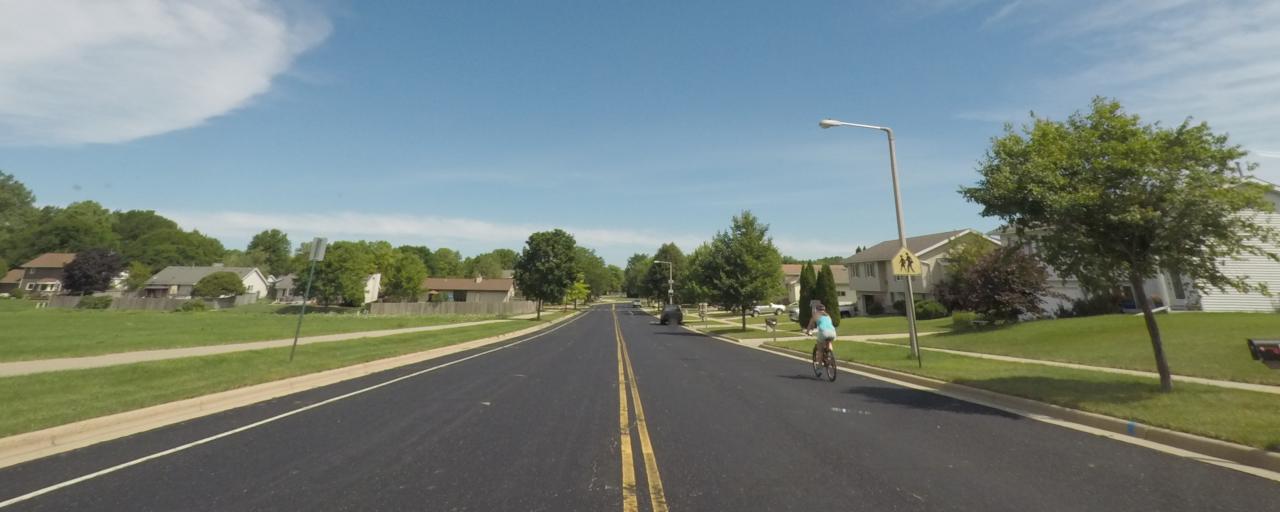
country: US
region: Wisconsin
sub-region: Dane County
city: McFarland
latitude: 43.0225
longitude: -89.2865
